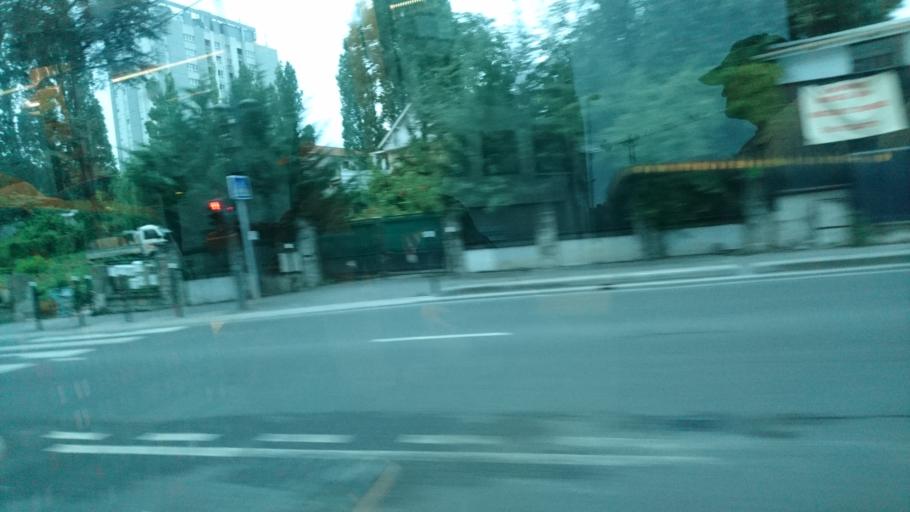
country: FR
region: Ile-de-France
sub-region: Departement de Seine-Saint-Denis
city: Pierrefitte-sur-Seine
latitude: 48.9711
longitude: 2.3661
